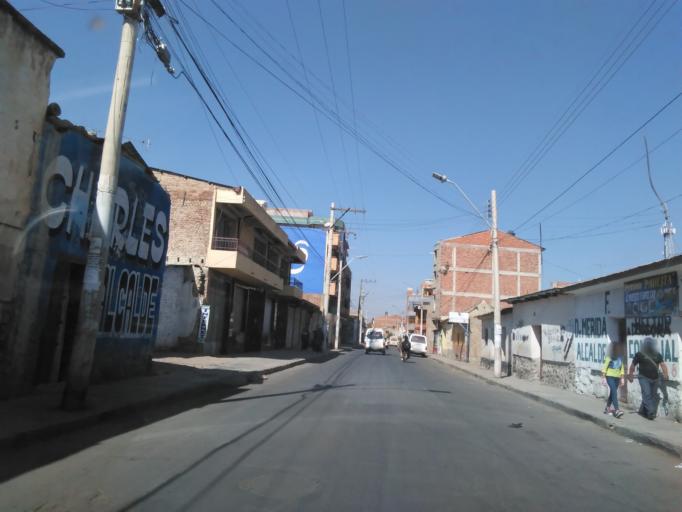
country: BO
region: Cochabamba
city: Sipe Sipe
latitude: -17.4003
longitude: -66.2797
